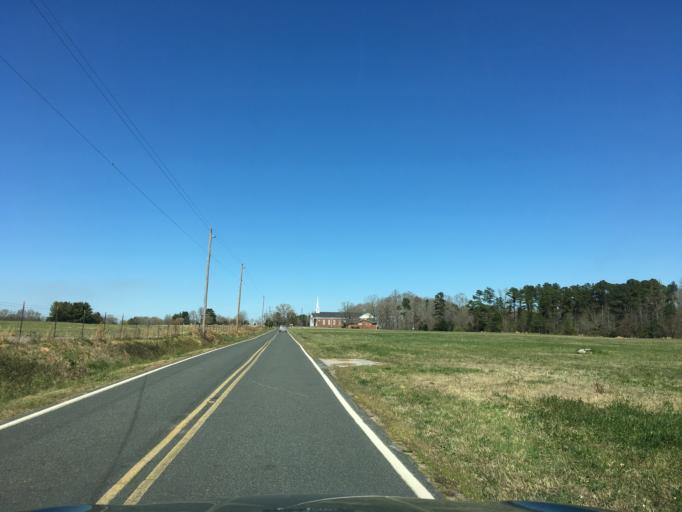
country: US
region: South Carolina
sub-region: Spartanburg County
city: Woodruff
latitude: 34.8116
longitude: -82.0850
